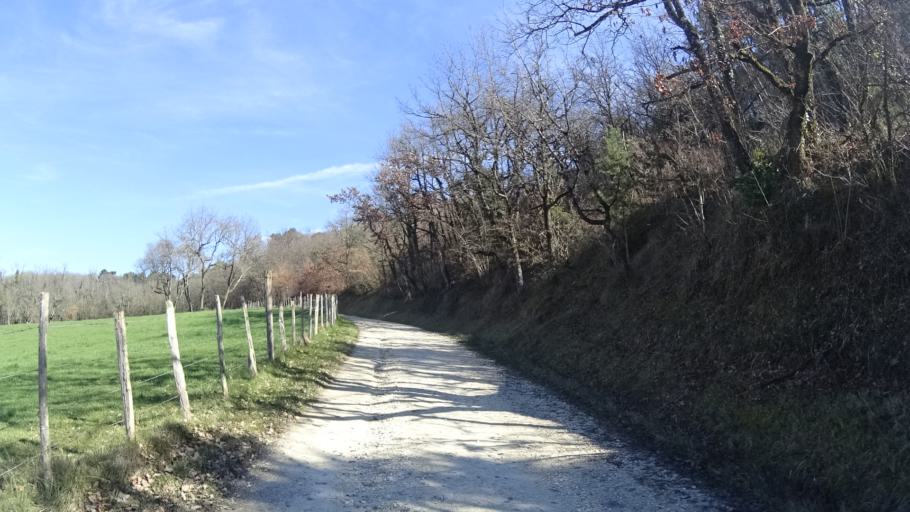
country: FR
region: Aquitaine
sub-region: Departement de la Dordogne
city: Riberac
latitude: 45.2113
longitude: 0.3276
